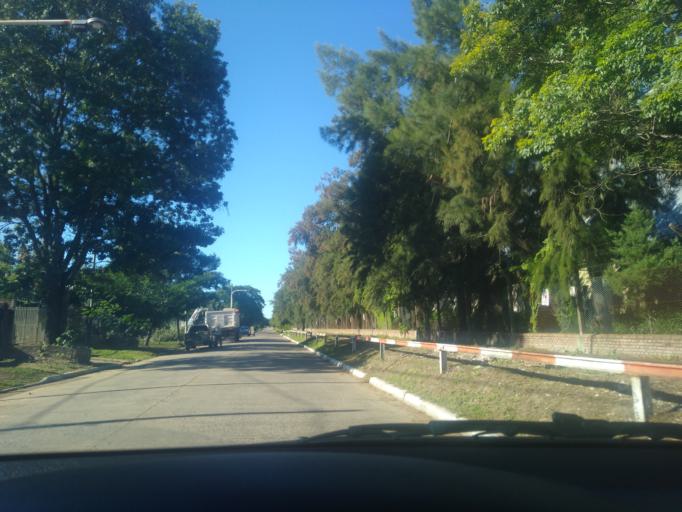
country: AR
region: Chaco
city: Puerto Vilelas
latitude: -27.5130
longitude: -58.9413
